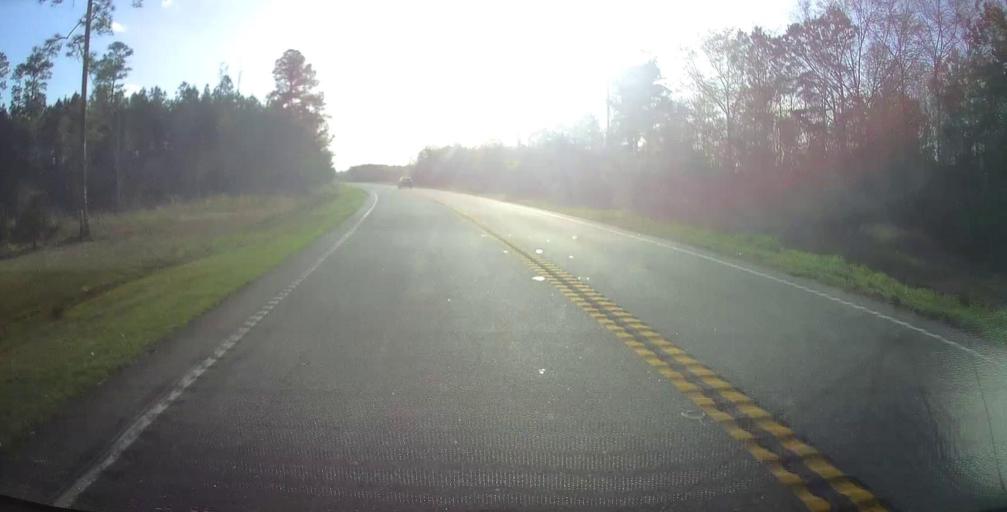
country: US
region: Georgia
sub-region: Evans County
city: Claxton
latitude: 32.1490
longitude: -82.0188
